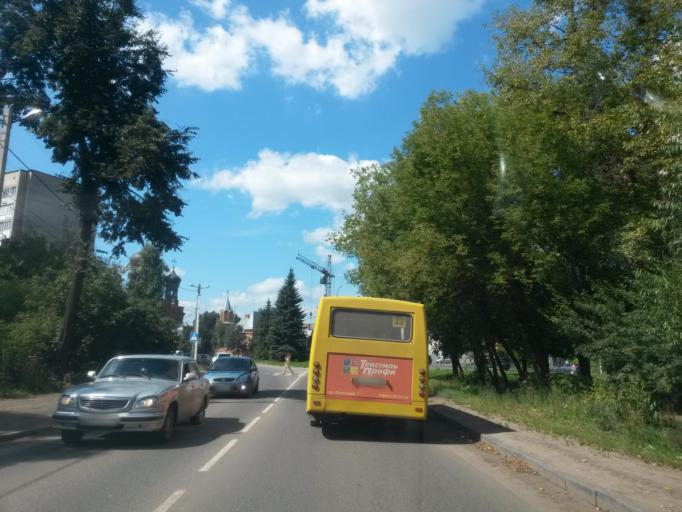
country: RU
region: Ivanovo
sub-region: Gorod Ivanovo
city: Ivanovo
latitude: 57.0101
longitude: 40.9934
